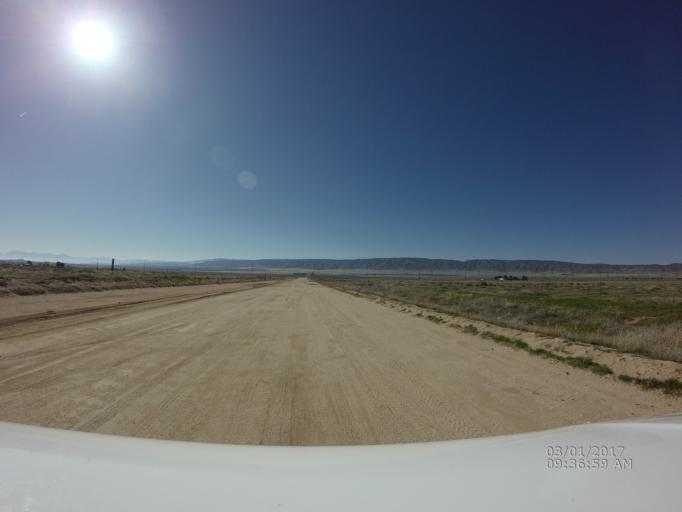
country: US
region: California
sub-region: Los Angeles County
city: Quartz Hill
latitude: 34.6929
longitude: -118.2717
